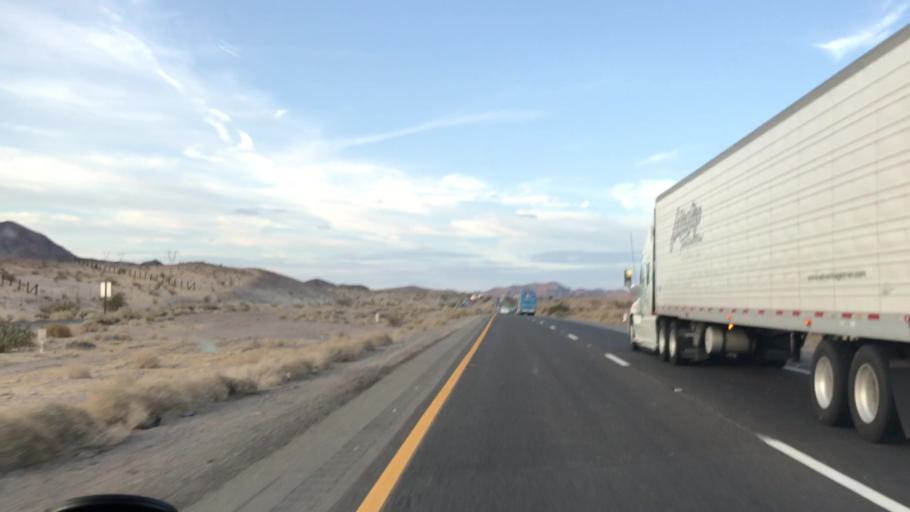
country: US
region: California
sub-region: San Bernardino County
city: Fort Irwin
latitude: 35.1195
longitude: -116.2327
